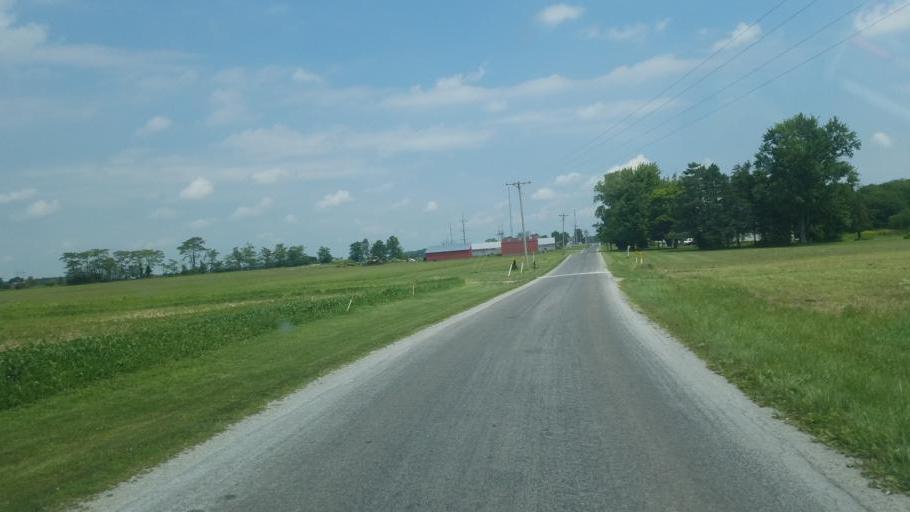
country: US
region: Ohio
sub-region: Hardin County
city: Kenton
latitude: 40.5822
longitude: -83.4540
